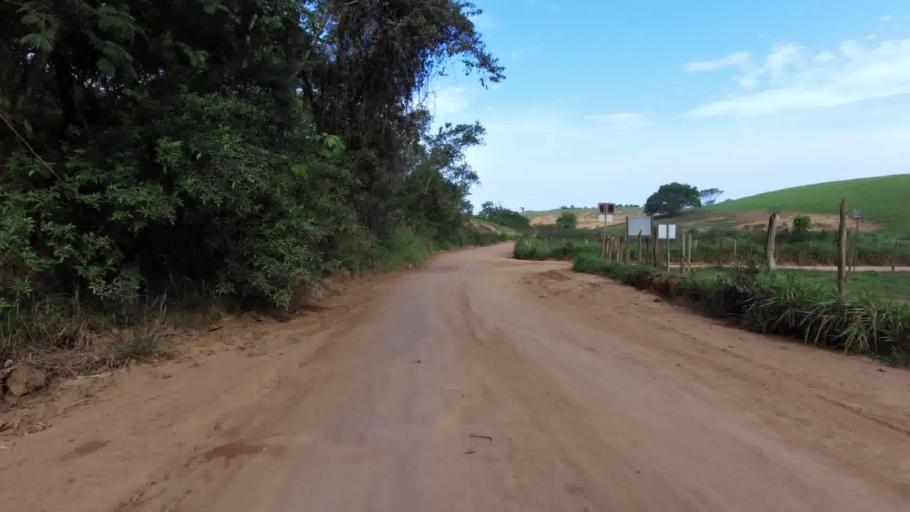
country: BR
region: Espirito Santo
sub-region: Piuma
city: Piuma
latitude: -20.8322
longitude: -40.7394
